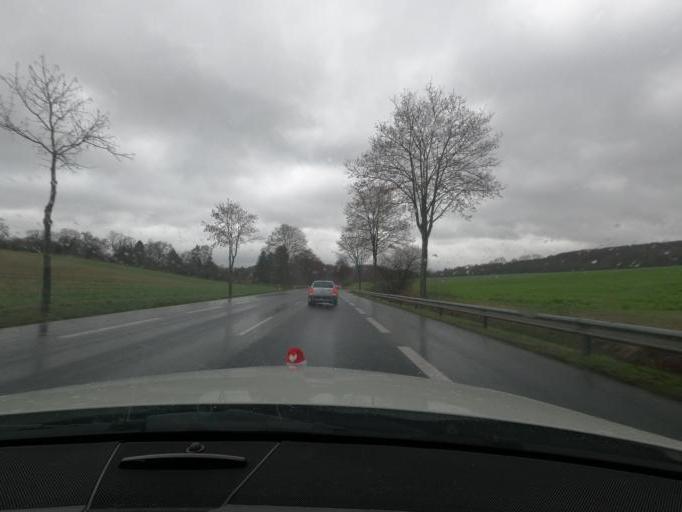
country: DE
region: Lower Saxony
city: Kreiensen
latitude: 51.8633
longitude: 9.9131
